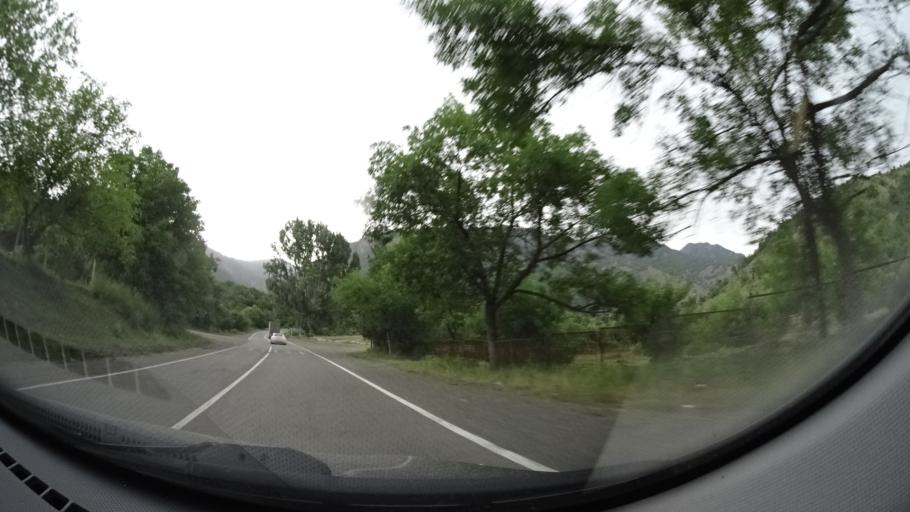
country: GE
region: Samtskhe-Javakheti
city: Borjomi
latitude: 41.7703
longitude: 43.2501
